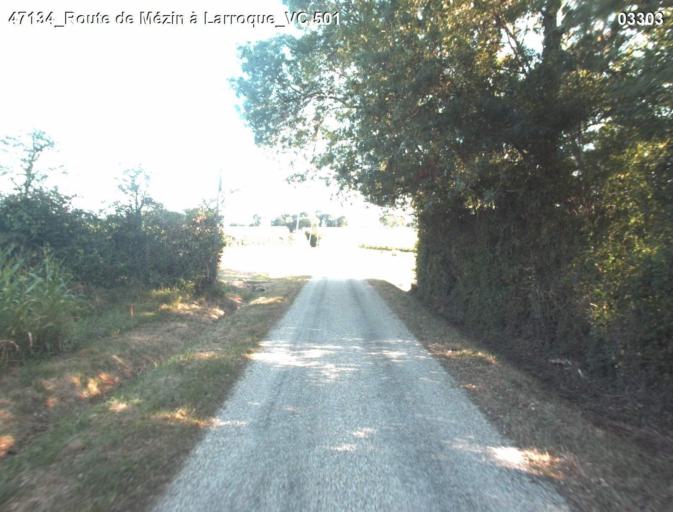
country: FR
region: Aquitaine
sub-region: Departement du Lot-et-Garonne
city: Mezin
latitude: 44.0245
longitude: 0.2700
